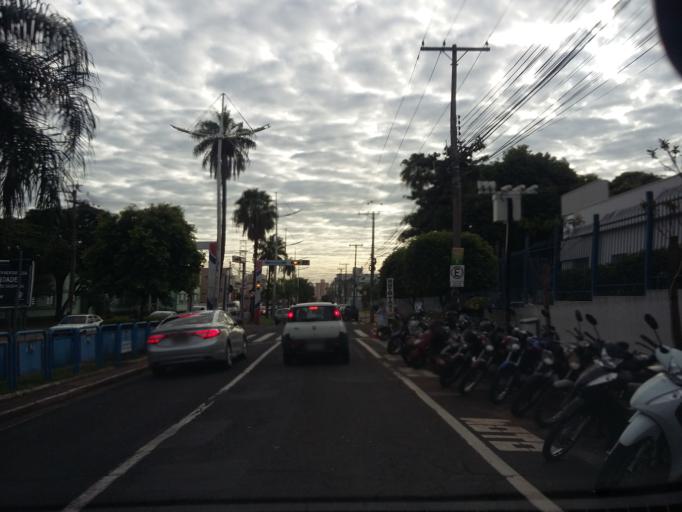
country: BR
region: Sao Paulo
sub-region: Sao Jose Do Rio Preto
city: Sao Jose do Rio Preto
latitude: -20.8285
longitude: -49.3965
